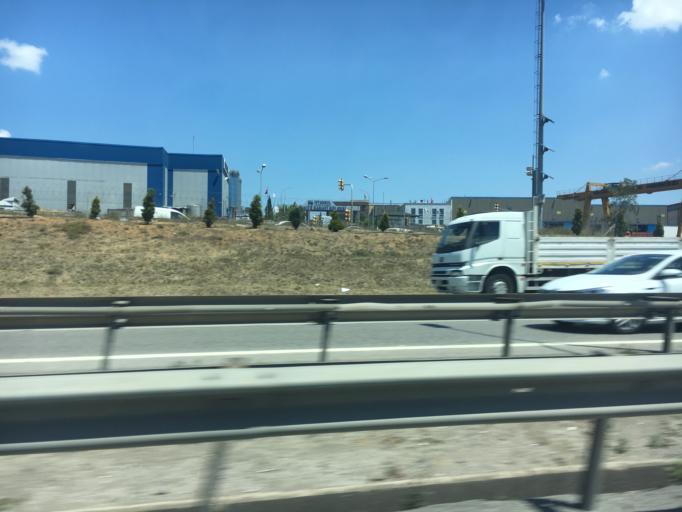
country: TR
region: Kocaeli
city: Balcik
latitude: 40.8811
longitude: 29.3808
